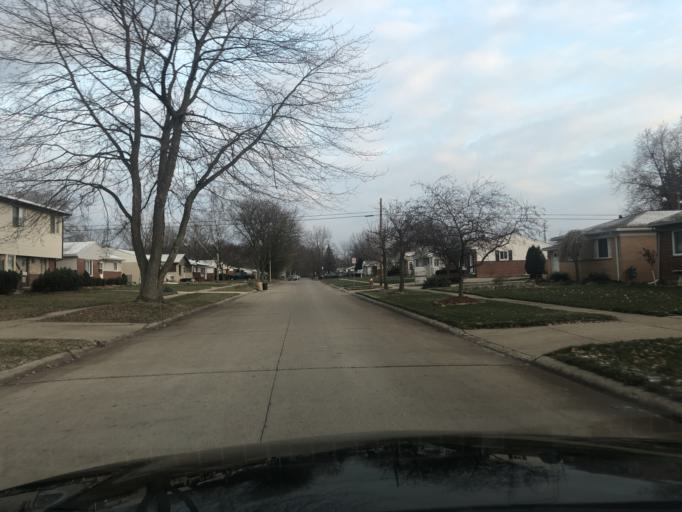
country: US
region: Michigan
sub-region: Wayne County
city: Romulus
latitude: 42.2337
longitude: -83.3809
